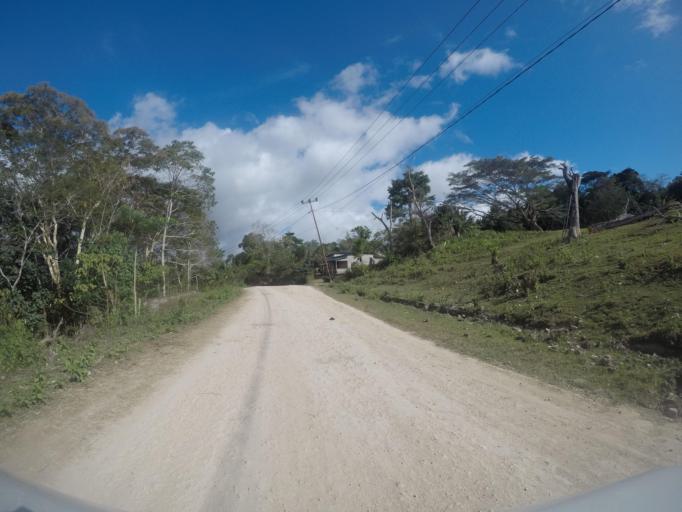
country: TL
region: Lautem
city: Lospalos
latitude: -8.5753
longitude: 126.8841
